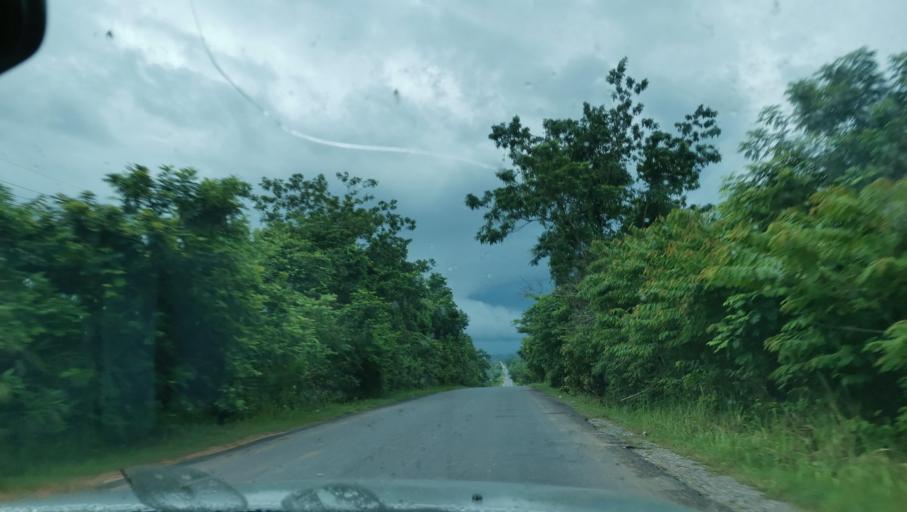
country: TH
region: Nakhon Phanom
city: Ban Phaeng
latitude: 17.8890
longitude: 104.3976
